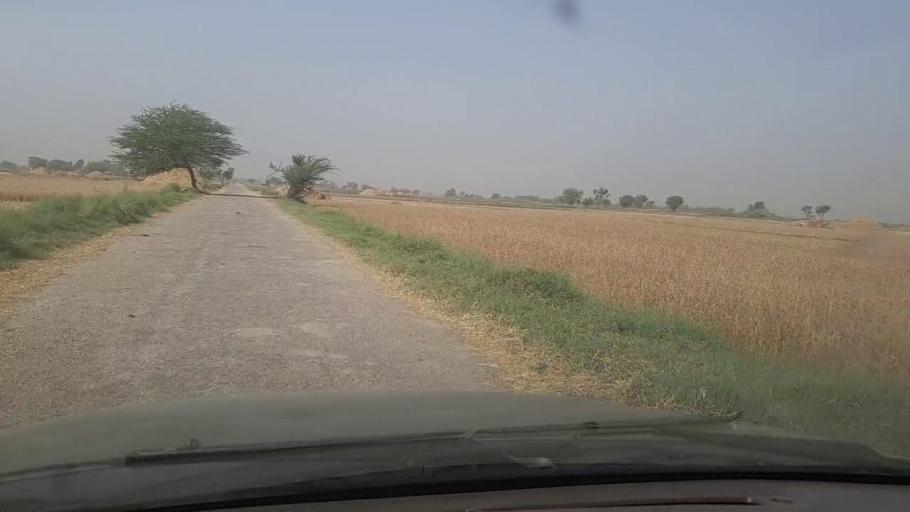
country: PK
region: Sindh
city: Garhi Yasin
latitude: 27.8850
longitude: 68.5735
